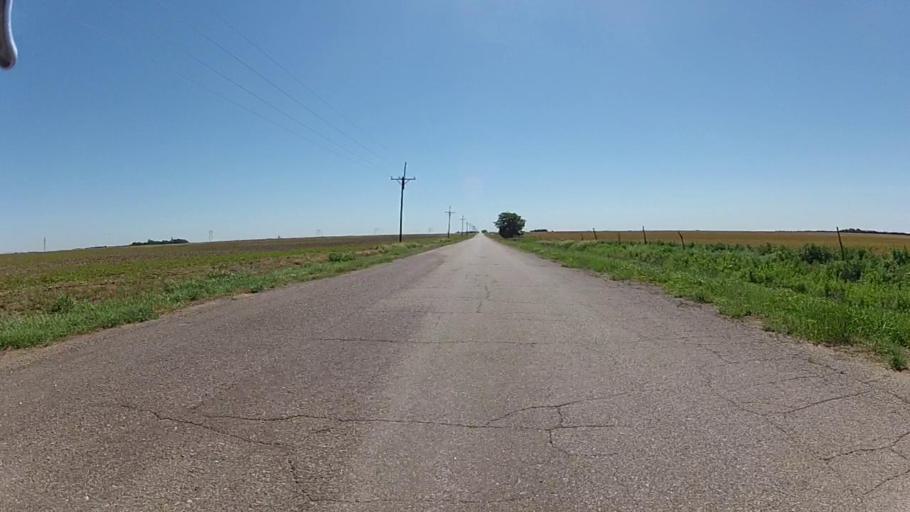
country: US
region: Kansas
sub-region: Kiowa County
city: Greensburg
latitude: 37.5866
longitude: -99.3526
